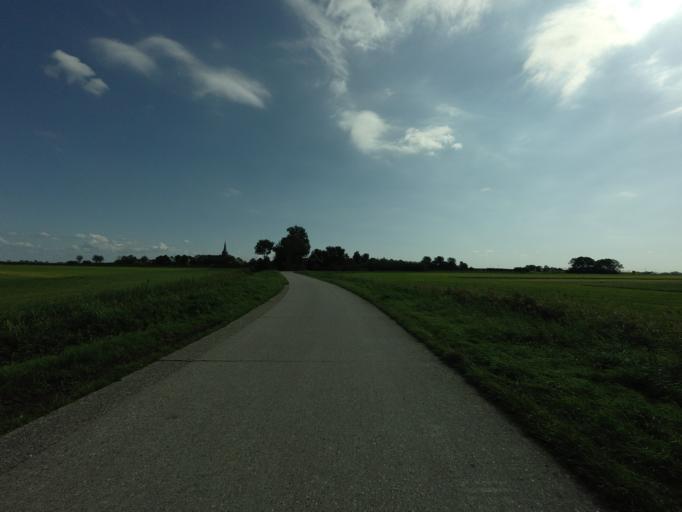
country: NL
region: Friesland
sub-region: Sudwest Fryslan
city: Scharnegoutum
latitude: 53.0793
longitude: 5.6316
